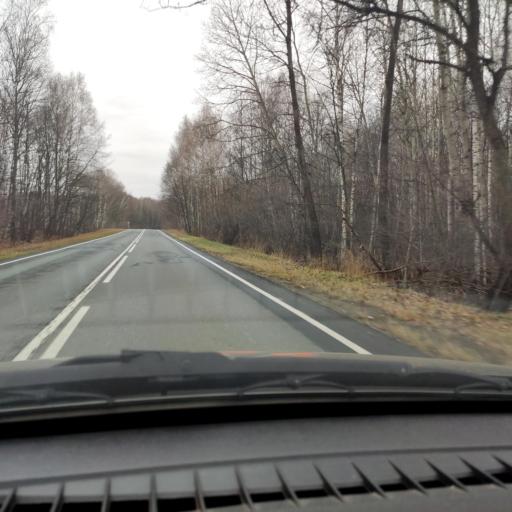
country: RU
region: Samara
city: Zhigulevsk
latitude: 53.3395
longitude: 49.5155
